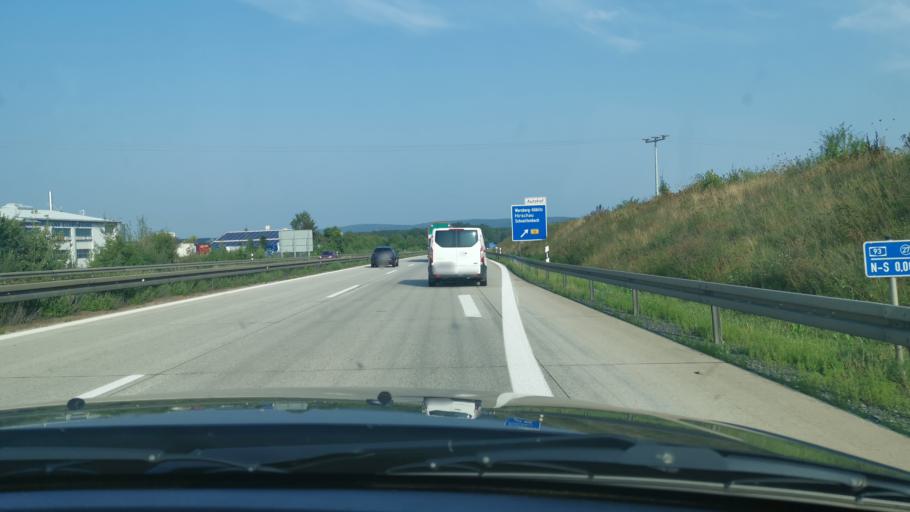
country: DE
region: Bavaria
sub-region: Upper Palatinate
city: Wernberg-Koblitz
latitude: 49.5298
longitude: 12.1450
